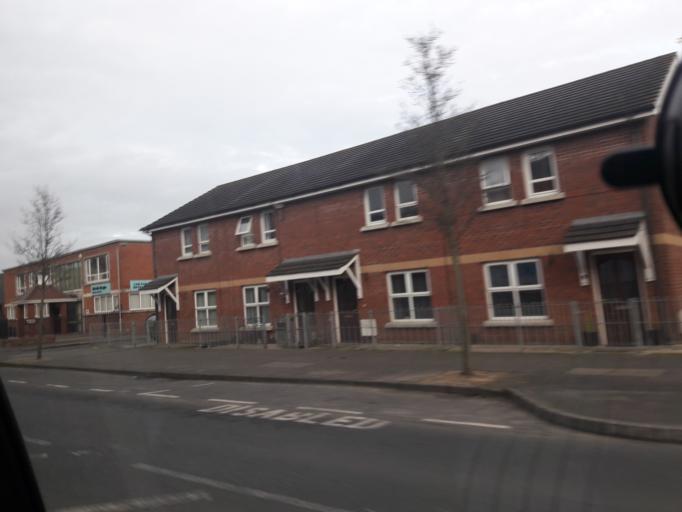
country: GB
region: Northern Ireland
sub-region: City of Belfast
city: Belfast
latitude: 54.6213
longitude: -5.9235
